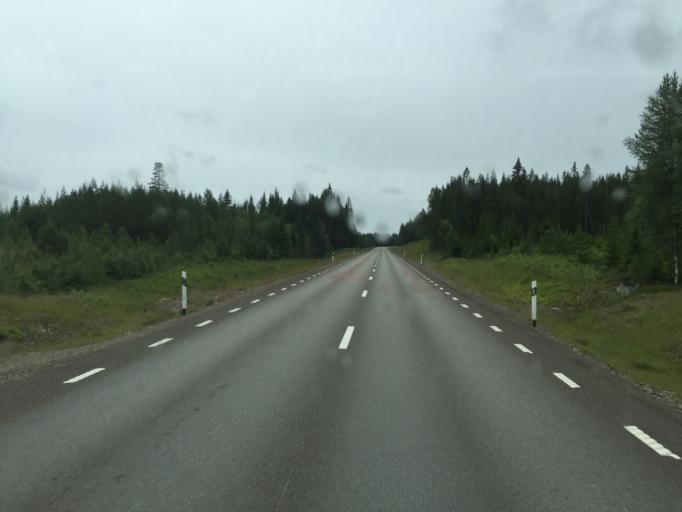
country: SE
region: Dalarna
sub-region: Malung-Saelens kommun
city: Malung
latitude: 60.5912
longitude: 13.5803
